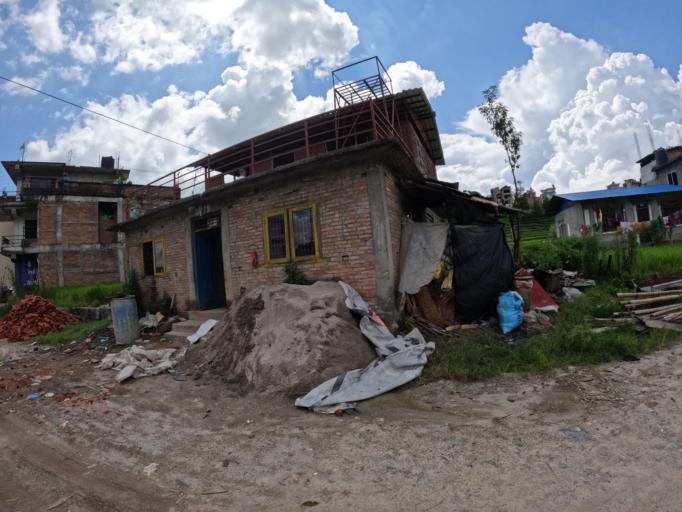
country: NP
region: Central Region
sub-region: Bagmati Zone
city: Kathmandu
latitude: 27.7775
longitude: 85.3289
